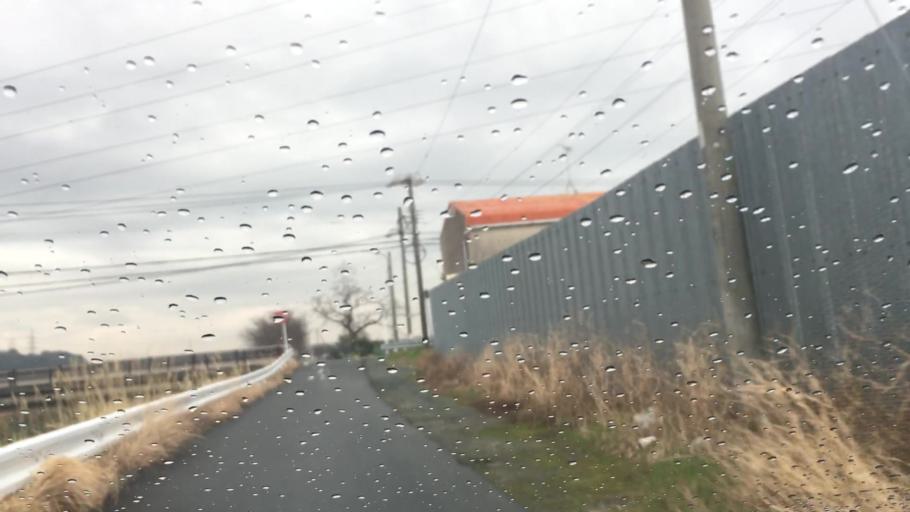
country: JP
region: Aichi
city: Toyohashi
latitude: 34.7066
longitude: 137.3915
